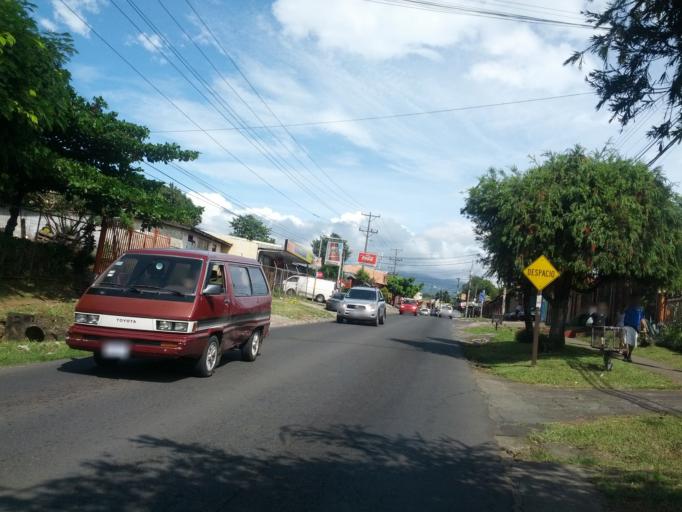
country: CR
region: Alajuela
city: Alajuela
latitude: 10.0188
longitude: -84.1942
